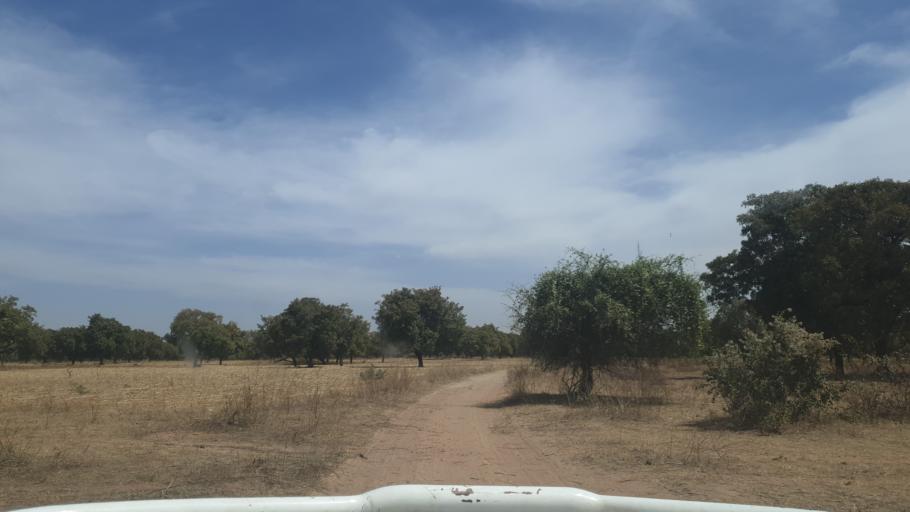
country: ML
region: Sikasso
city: Yorosso
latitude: 12.2865
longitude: -4.6789
